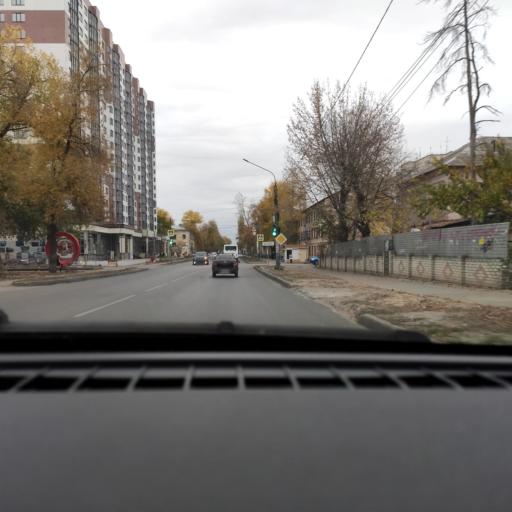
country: RU
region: Voronezj
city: Voronezh
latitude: 51.7230
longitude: 39.2654
